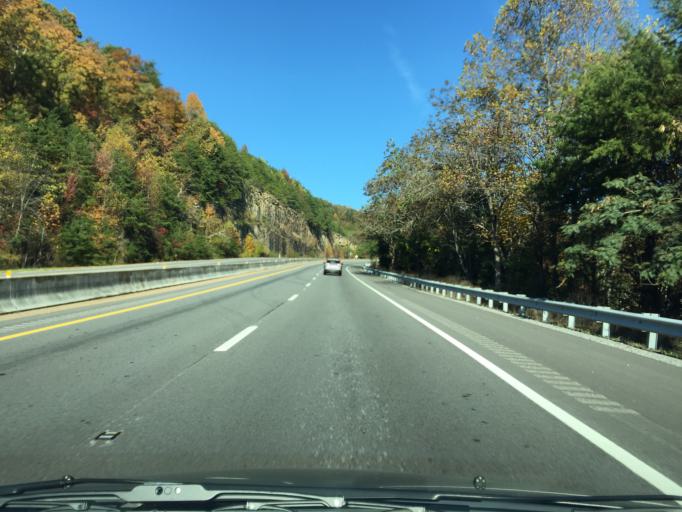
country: US
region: Tennessee
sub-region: Hamilton County
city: Sale Creek
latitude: 35.3250
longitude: -85.1611
